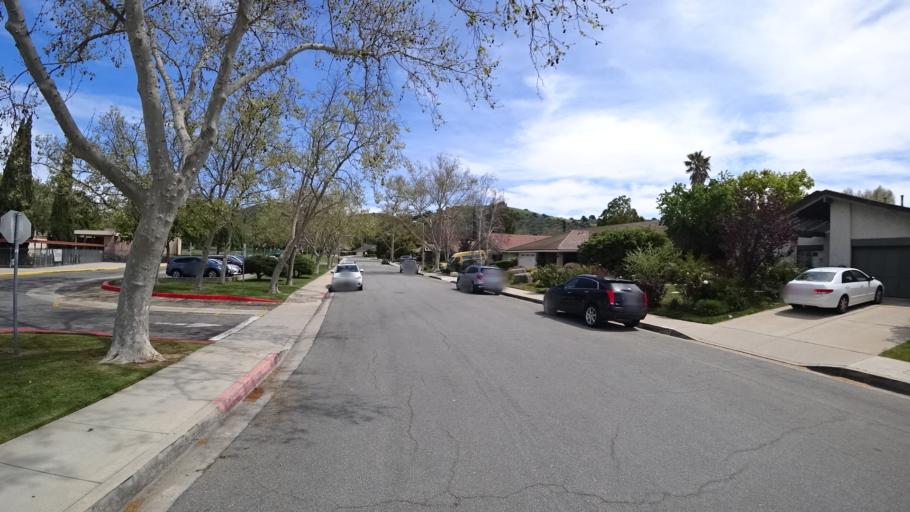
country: US
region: California
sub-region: Ventura County
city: Thousand Oaks
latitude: 34.1672
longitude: -118.8268
